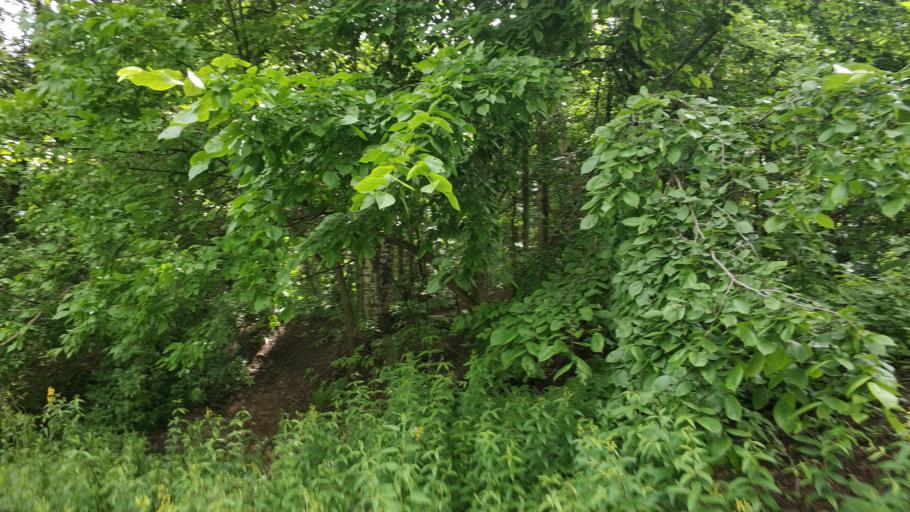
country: RU
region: Moskovskaya
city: Novogireyevo
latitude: 55.7423
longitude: 37.8132
